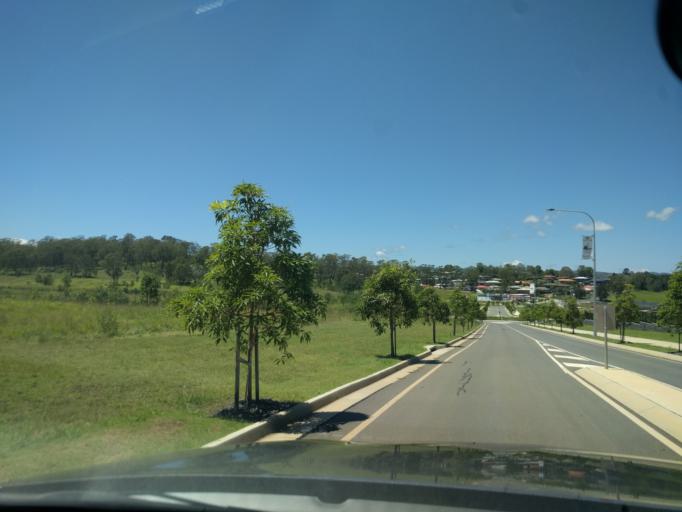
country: AU
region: Queensland
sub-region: Logan
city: Cedar Vale
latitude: -27.9895
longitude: 153.0128
